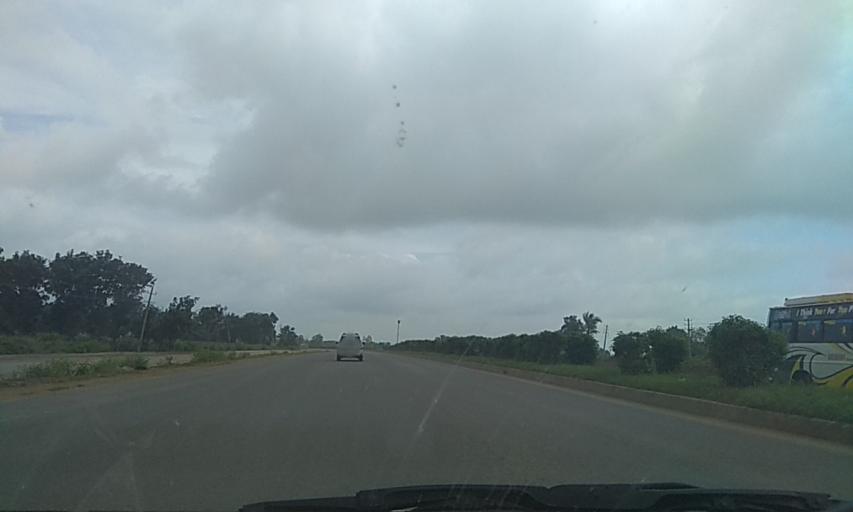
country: IN
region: Karnataka
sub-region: Dharwad
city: Kundgol
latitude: 15.1746
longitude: 75.1399
